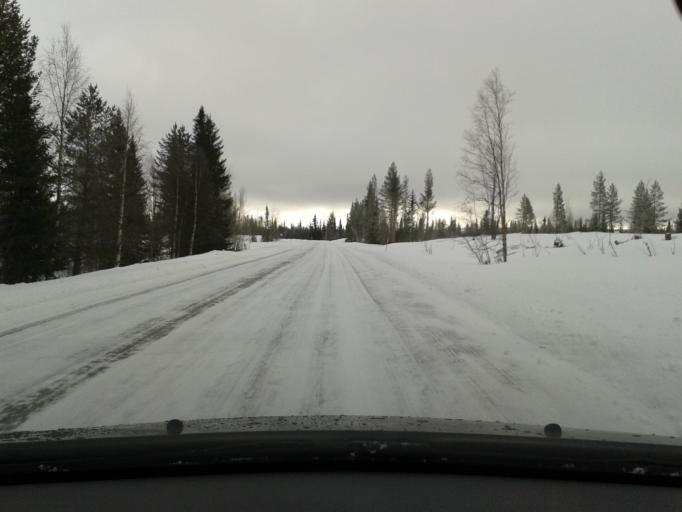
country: SE
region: Vaesterbotten
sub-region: Vilhelmina Kommun
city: Sjoberg
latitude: 64.8116
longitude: 15.9750
